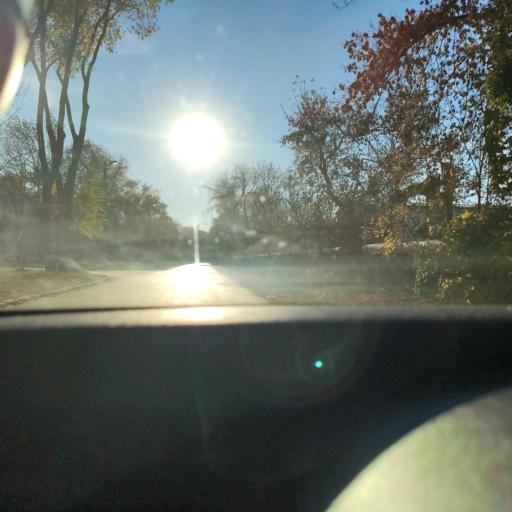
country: RU
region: Samara
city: Smyshlyayevka
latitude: 53.1902
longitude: 50.2910
